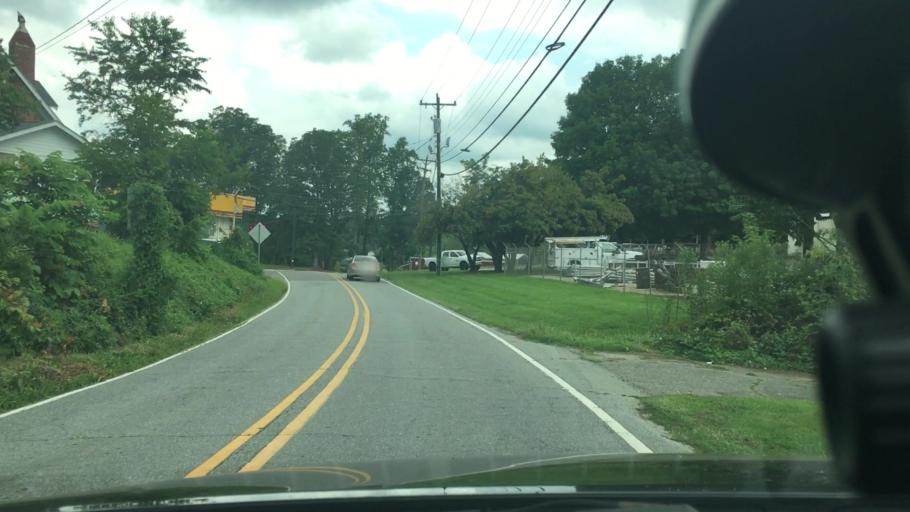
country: US
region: North Carolina
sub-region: McDowell County
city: West Marion
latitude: 35.6673
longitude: -82.0177
